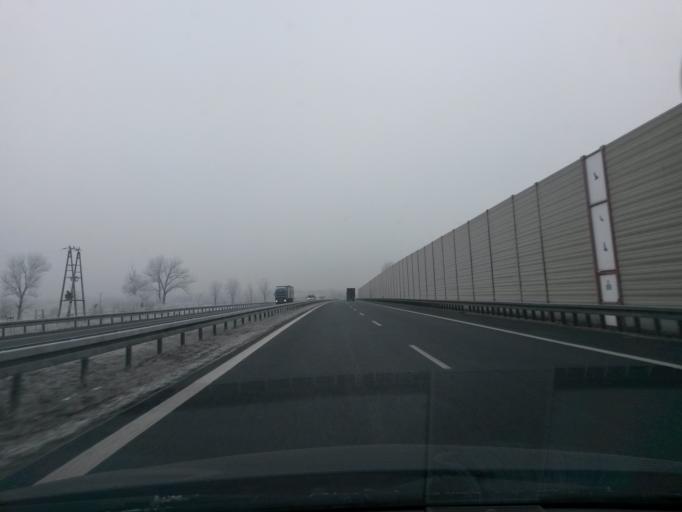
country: PL
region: Greater Poland Voivodeship
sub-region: Powiat gnieznienski
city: Lubowo
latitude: 52.4743
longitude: 17.4107
